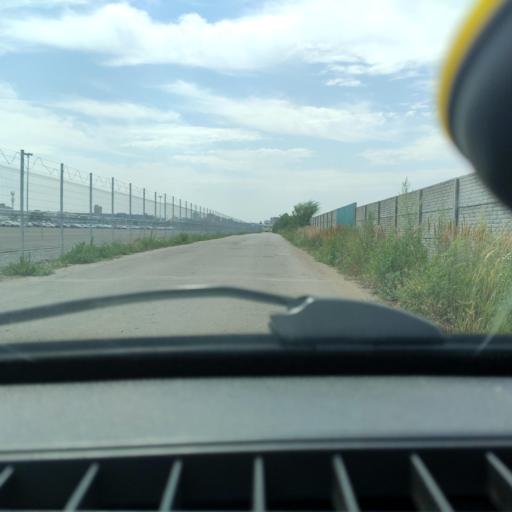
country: RU
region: Samara
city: Tol'yatti
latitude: 53.5598
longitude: 49.3432
